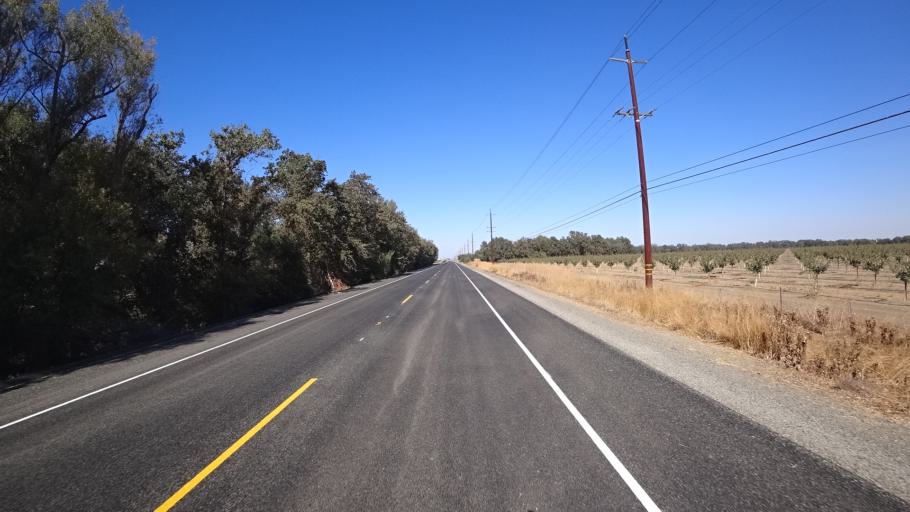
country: US
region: California
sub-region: Yolo County
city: Woodland
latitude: 38.6279
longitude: -121.7296
